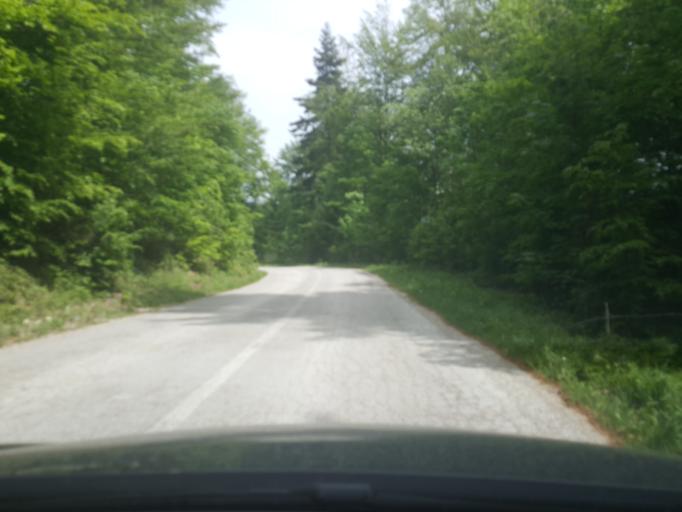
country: RS
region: Central Serbia
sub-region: Zlatiborski Okrug
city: Bajina Basta
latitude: 43.9118
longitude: 19.5010
